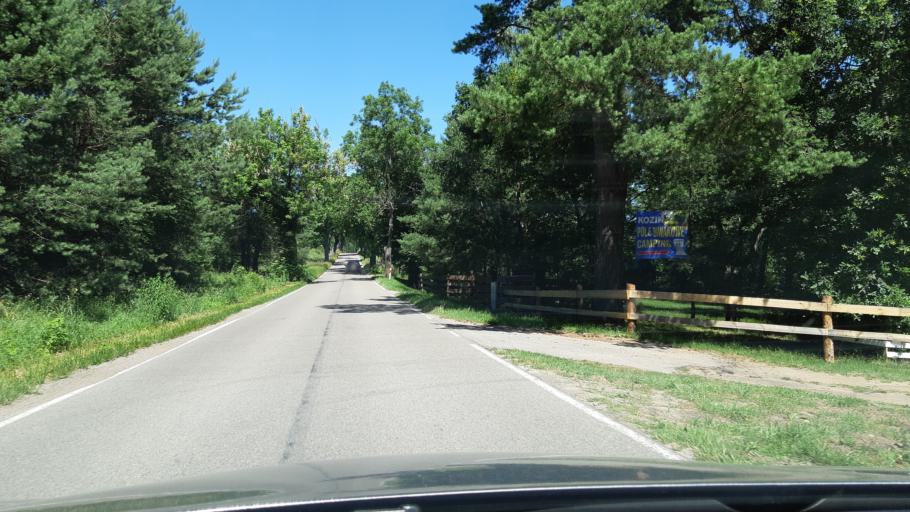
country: PL
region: Warmian-Masurian Voivodeship
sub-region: Powiat gizycki
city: Gizycko
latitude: 53.9348
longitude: 21.7174
